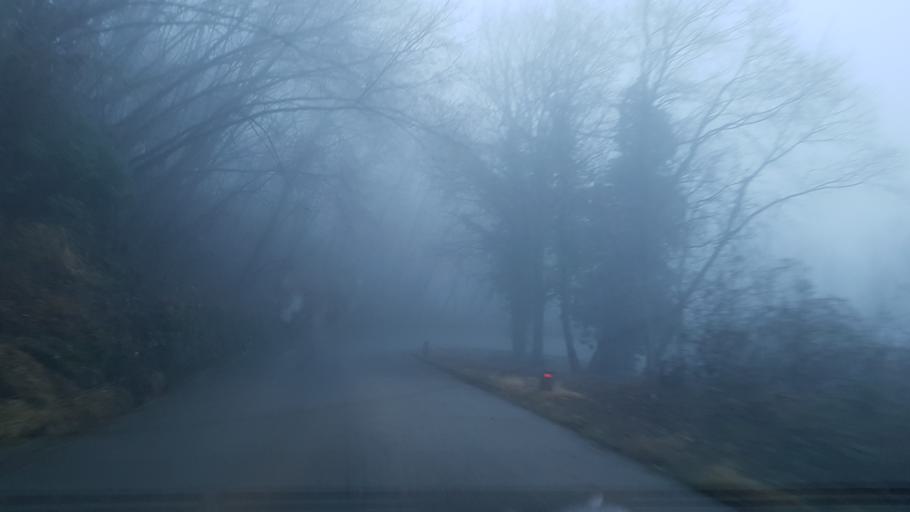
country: IT
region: Friuli Venezia Giulia
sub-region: Provincia di Udine
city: San Leonardo
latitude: 46.0912
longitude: 13.5509
